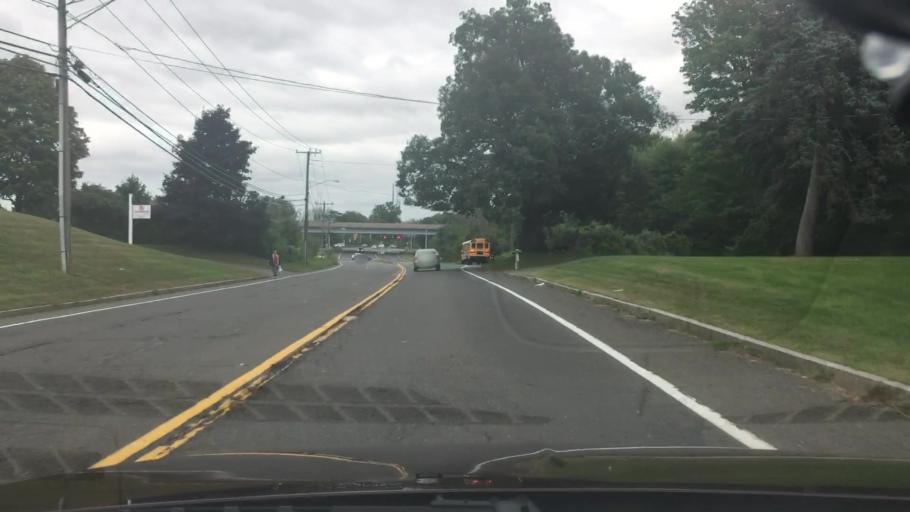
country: US
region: Connecticut
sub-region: Hartford County
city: East Hartford
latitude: 41.7916
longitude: -72.5743
